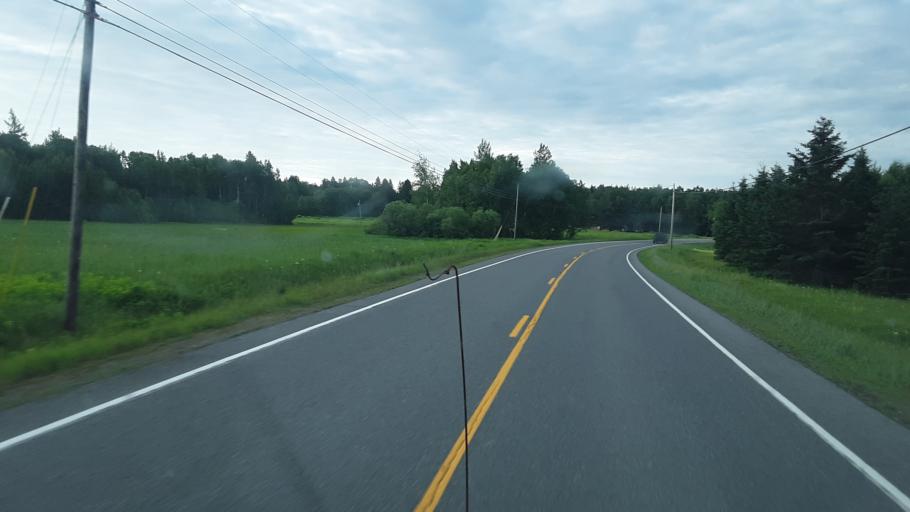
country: US
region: Maine
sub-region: Aroostook County
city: Presque Isle
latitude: 46.5146
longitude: -68.3545
